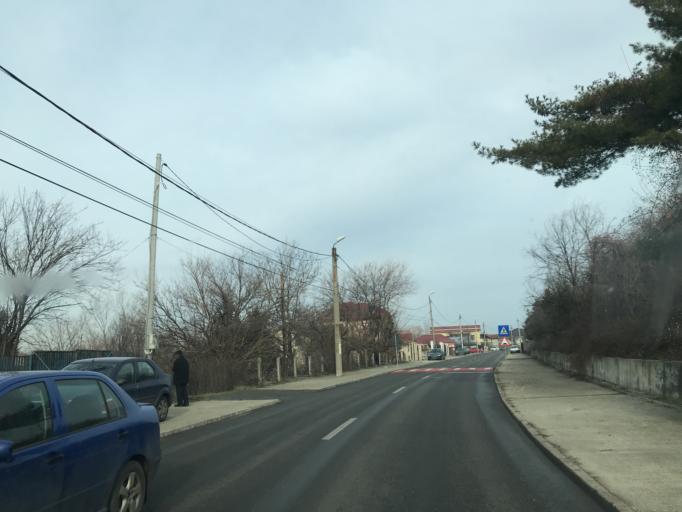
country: RO
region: Olt
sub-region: Municipiul Slatina
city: Slatina
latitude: 44.4372
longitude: 24.3690
